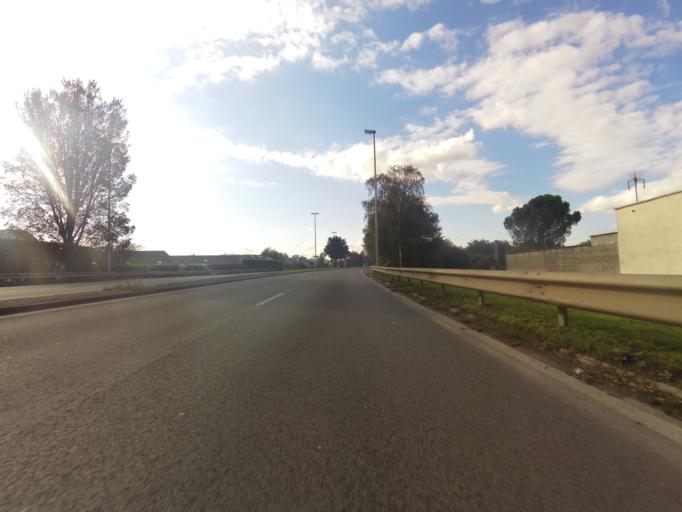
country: FR
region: Nord-Pas-de-Calais
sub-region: Departement du Nord
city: Neuville-Saint-Remy
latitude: 50.1748
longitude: 3.2153
